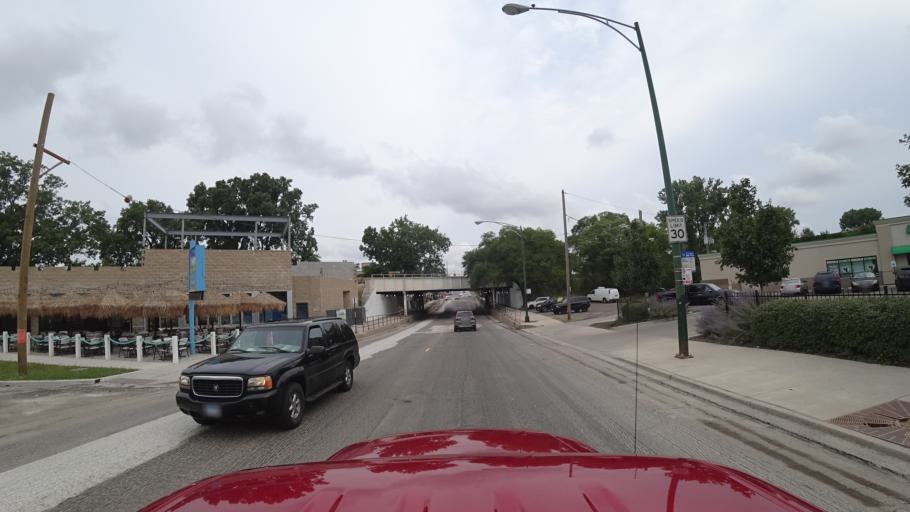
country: US
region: Illinois
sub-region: Cook County
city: Chicago
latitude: 41.8321
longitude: -87.6753
